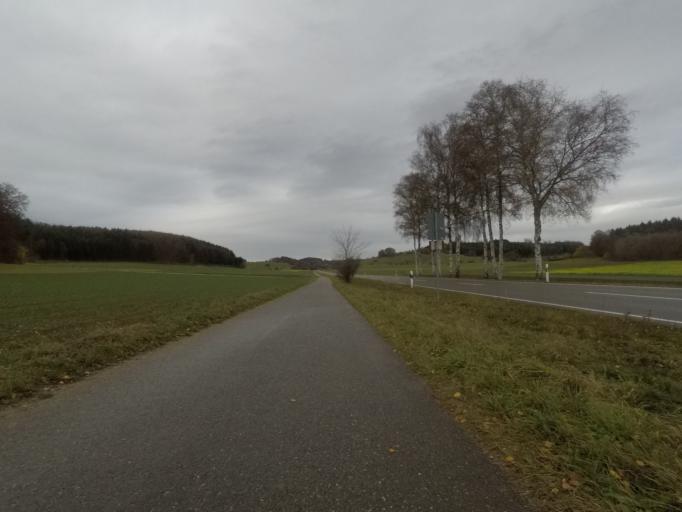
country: DE
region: Baden-Wuerttemberg
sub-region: Tuebingen Region
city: Sankt Johann
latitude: 48.4106
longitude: 9.2865
